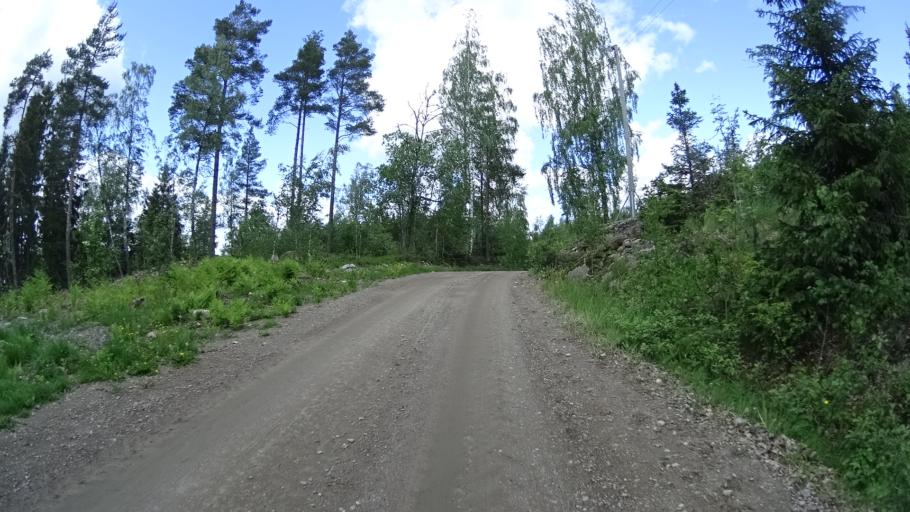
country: FI
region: Uusimaa
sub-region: Raaseporin
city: Karis
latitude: 60.1428
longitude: 23.6185
